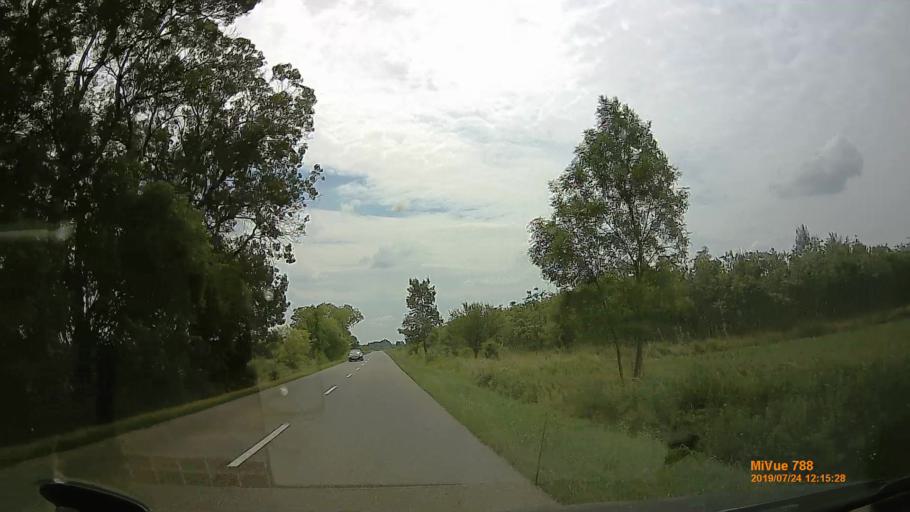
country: HU
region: Szabolcs-Szatmar-Bereg
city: Vasarosnameny
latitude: 48.1840
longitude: 22.3452
